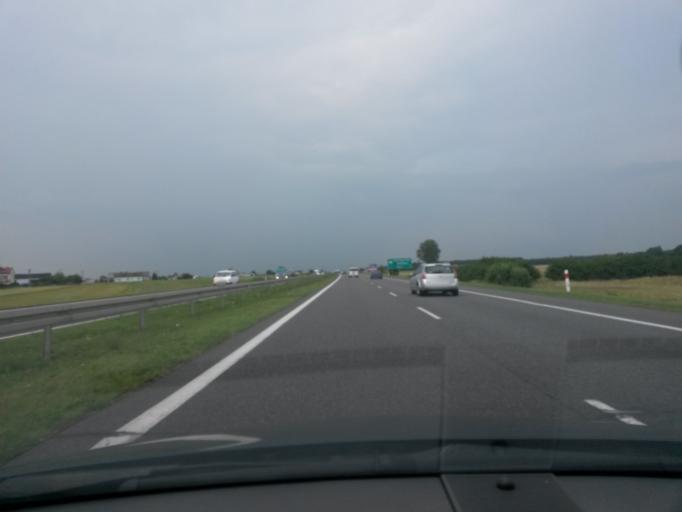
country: PL
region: Lodz Voivodeship
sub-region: Powiat piotrkowski
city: Wola Krzysztoporska
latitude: 51.3793
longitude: 19.6231
